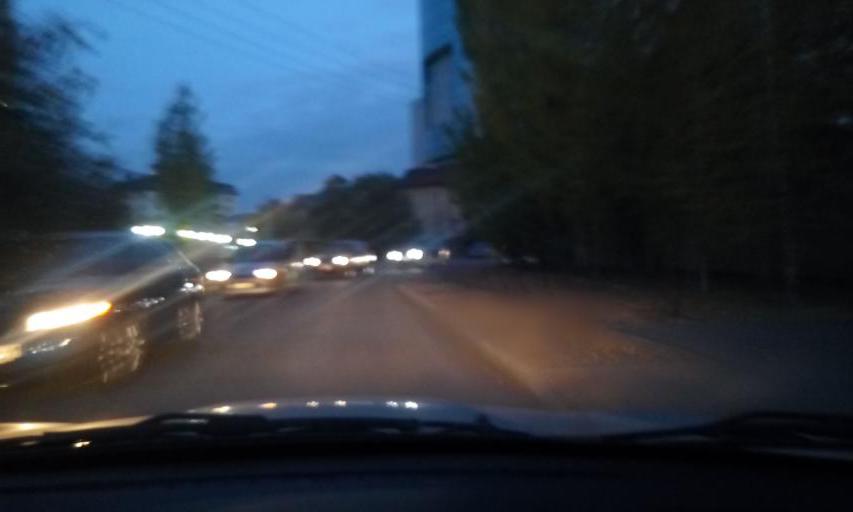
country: KZ
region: Astana Qalasy
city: Astana
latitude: 51.1370
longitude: 71.4300
